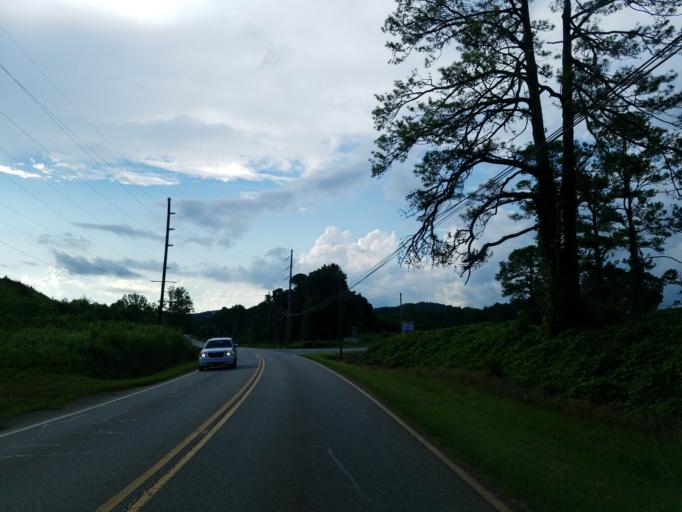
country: US
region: Georgia
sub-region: Bartow County
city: Emerson
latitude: 34.1421
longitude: -84.7656
